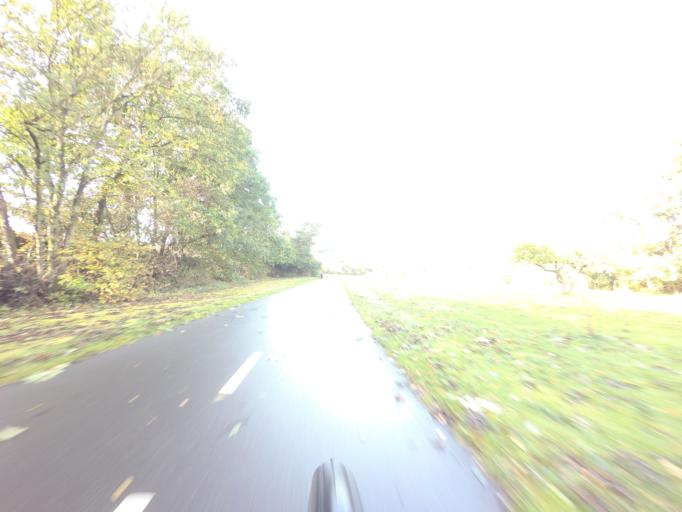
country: DK
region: Central Jutland
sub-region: Viborg Kommune
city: Viborg
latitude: 56.4214
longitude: 9.4453
